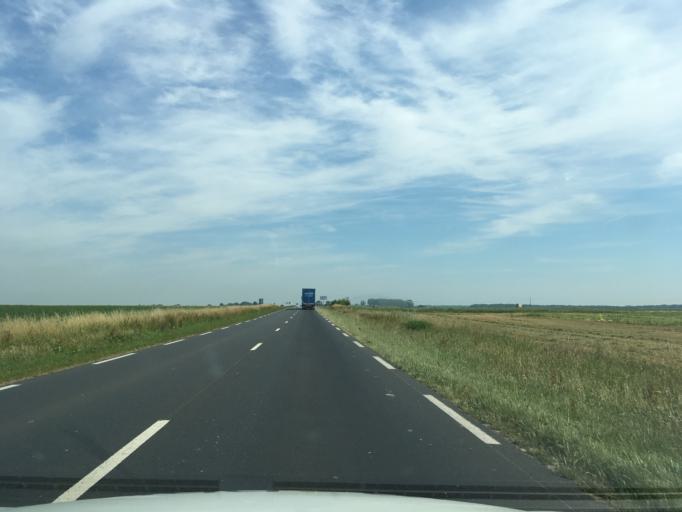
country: FR
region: Picardie
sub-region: Departement de la Somme
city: Roye
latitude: 49.7387
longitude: 2.8085
